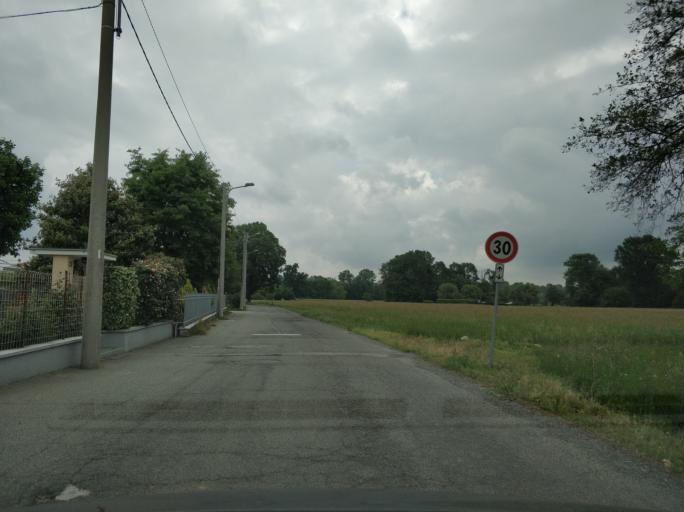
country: IT
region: Piedmont
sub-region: Provincia di Torino
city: Nole
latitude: 45.2433
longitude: 7.5825
